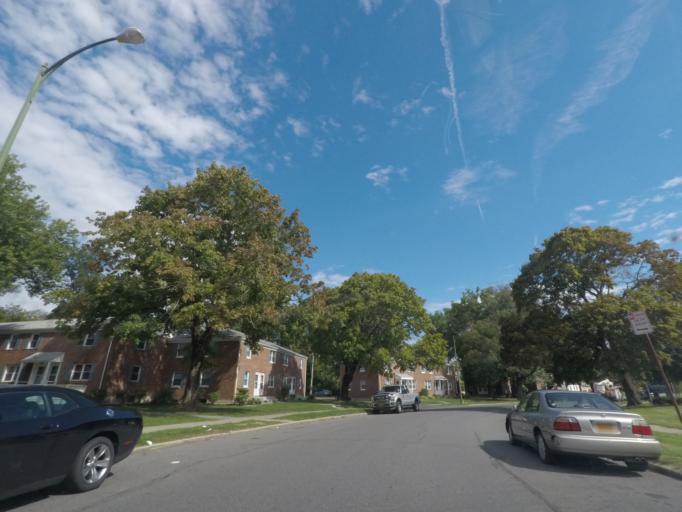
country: US
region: New York
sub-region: Albany County
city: Delmar
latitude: 42.6540
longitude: -73.8100
